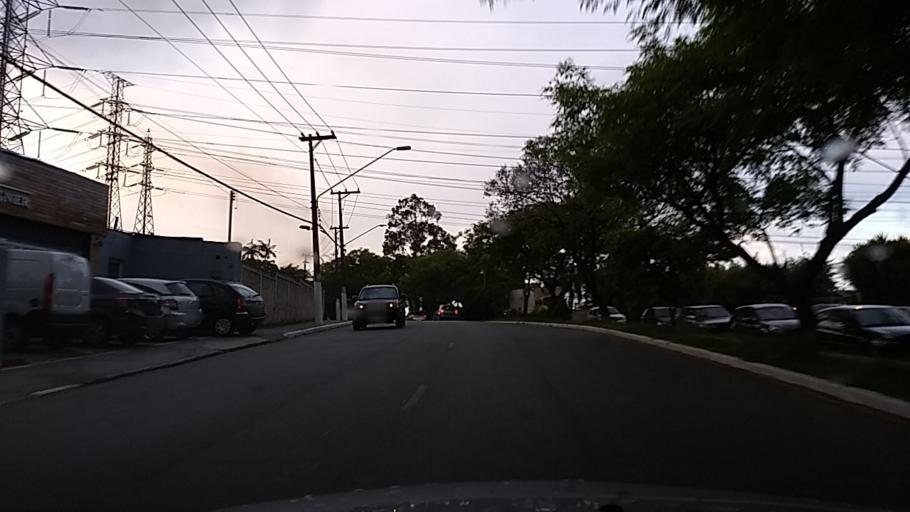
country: BR
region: Sao Paulo
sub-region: Osasco
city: Osasco
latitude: -23.4978
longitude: -46.7356
